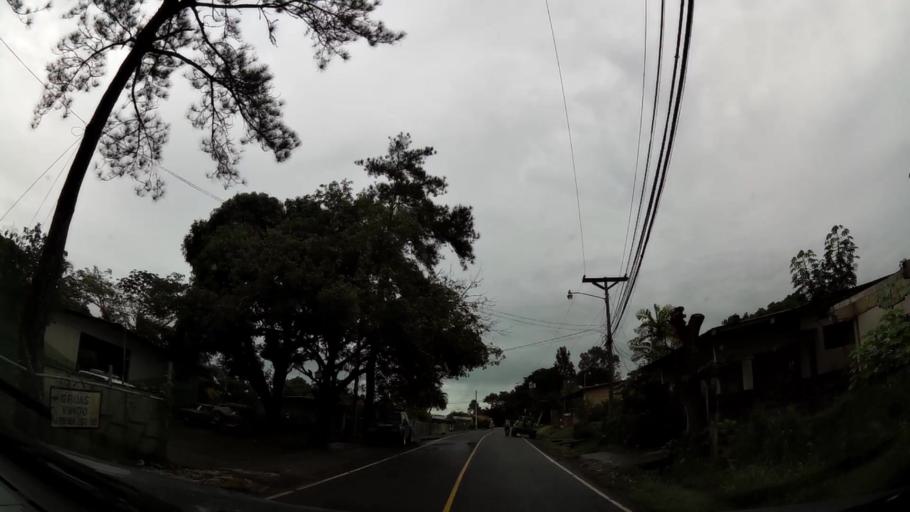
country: PA
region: Veraguas
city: Santiago de Veraguas
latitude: 8.1057
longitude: -80.9821
